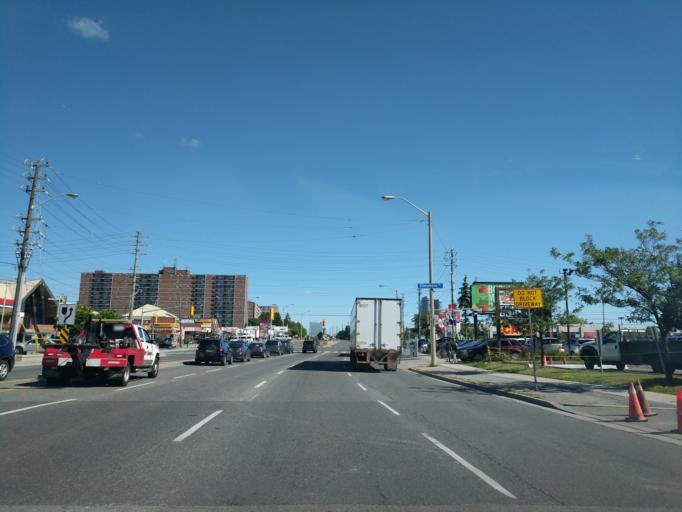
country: CA
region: Ontario
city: Scarborough
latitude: 43.7650
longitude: -79.2808
